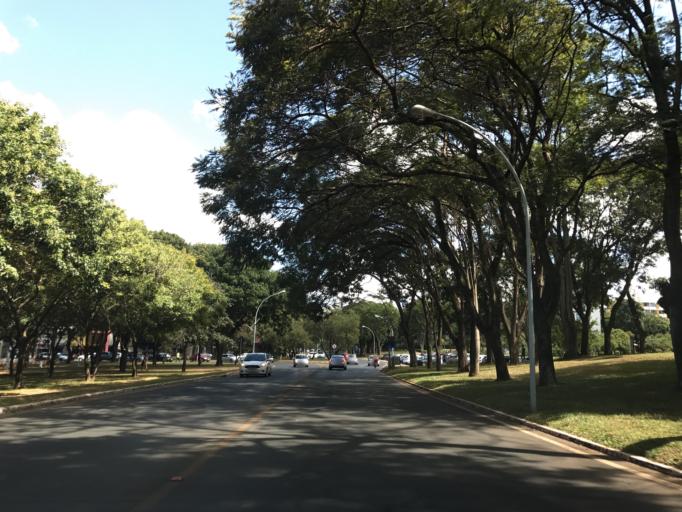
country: BR
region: Federal District
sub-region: Brasilia
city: Brasilia
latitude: -15.8330
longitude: -47.9170
